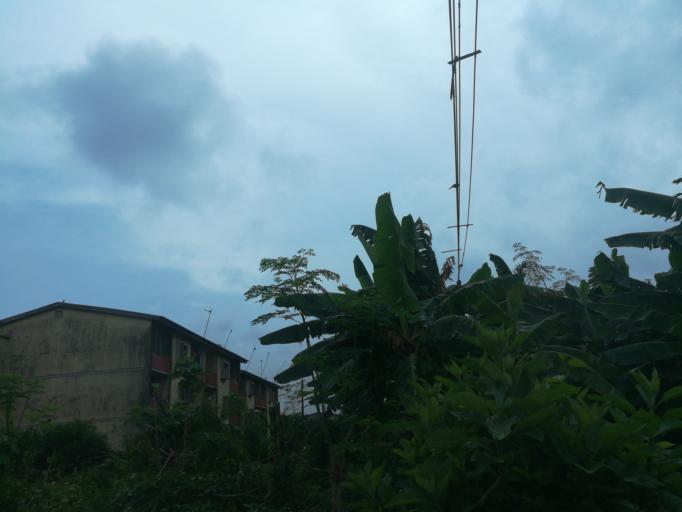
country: NG
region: Lagos
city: Oshodi
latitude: 6.5706
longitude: 3.3552
